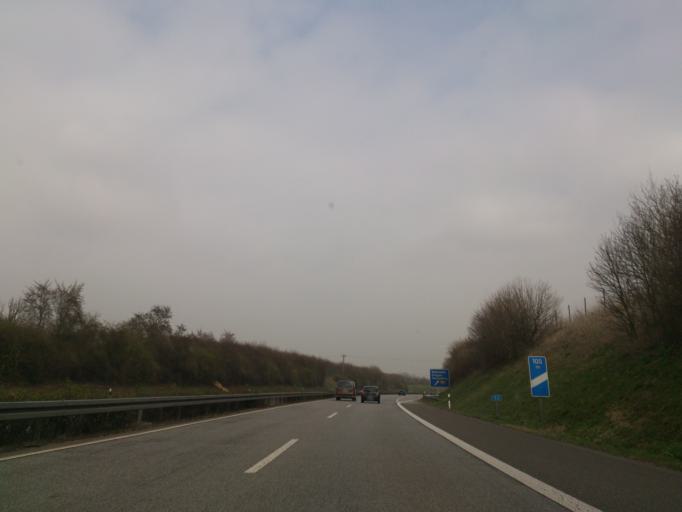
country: DE
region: North Rhine-Westphalia
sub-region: Regierungsbezirk Dusseldorf
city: Niederkruchten
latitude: 51.2054
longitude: 6.2064
